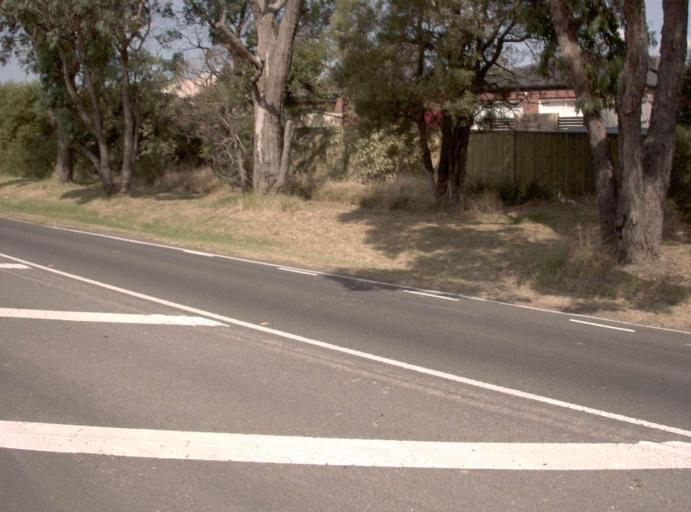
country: AU
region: Victoria
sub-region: Knox
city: Ferntree Gully
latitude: -37.9057
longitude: 145.2809
